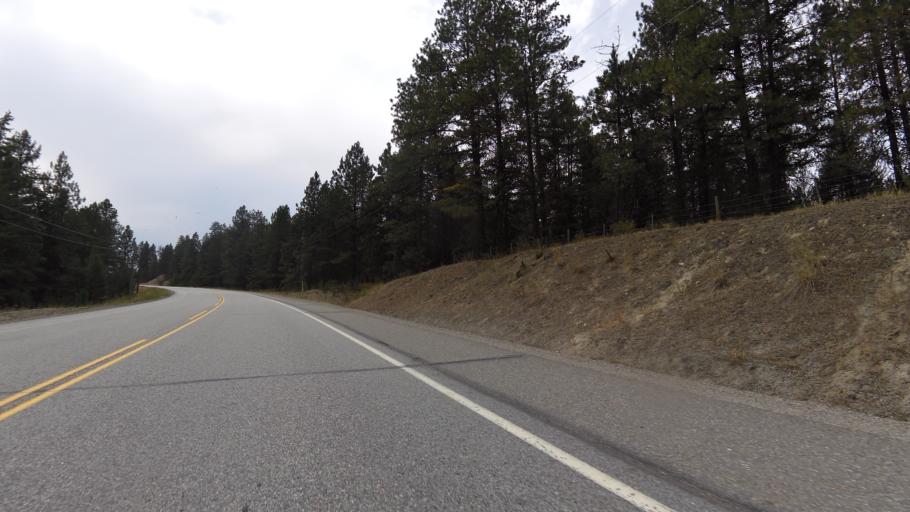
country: US
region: Washington
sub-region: Okanogan County
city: Oroville
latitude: 49.0094
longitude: -119.3091
